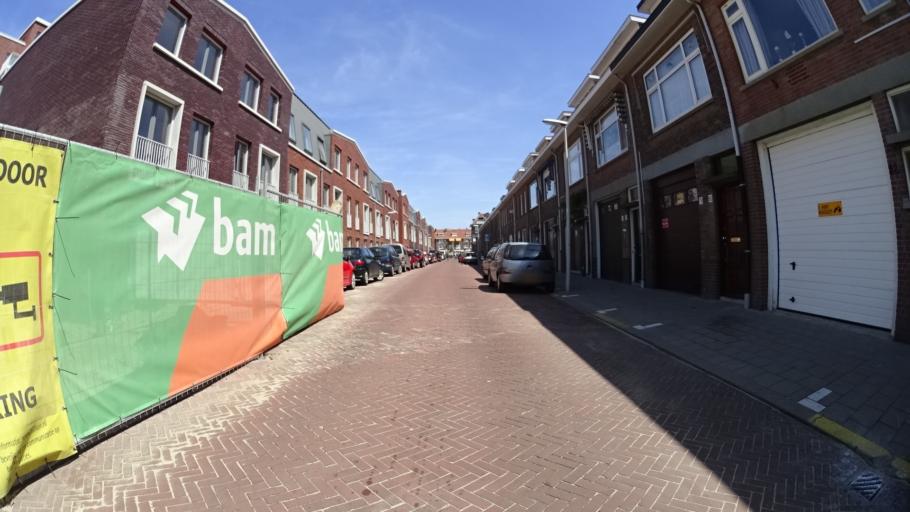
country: NL
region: South Holland
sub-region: Gemeente Den Haag
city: Scheveningen
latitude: 52.0960
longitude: 4.2686
